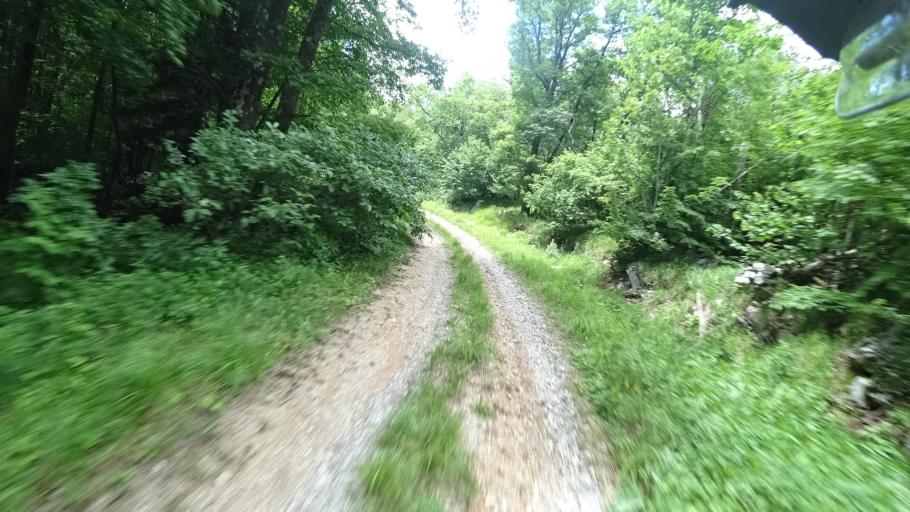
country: HR
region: Primorsko-Goranska
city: Bribir
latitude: 45.2162
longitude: 14.7465
